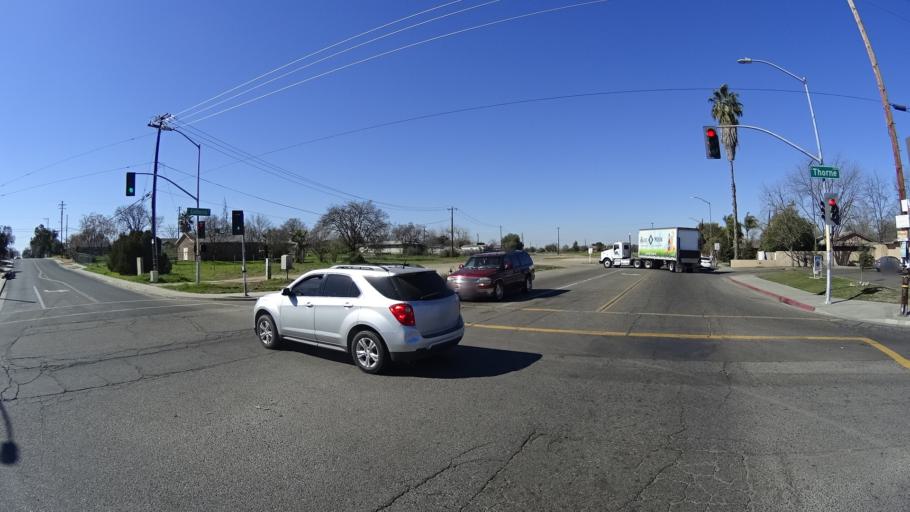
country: US
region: California
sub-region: Fresno County
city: West Park
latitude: 36.7208
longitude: -119.8133
